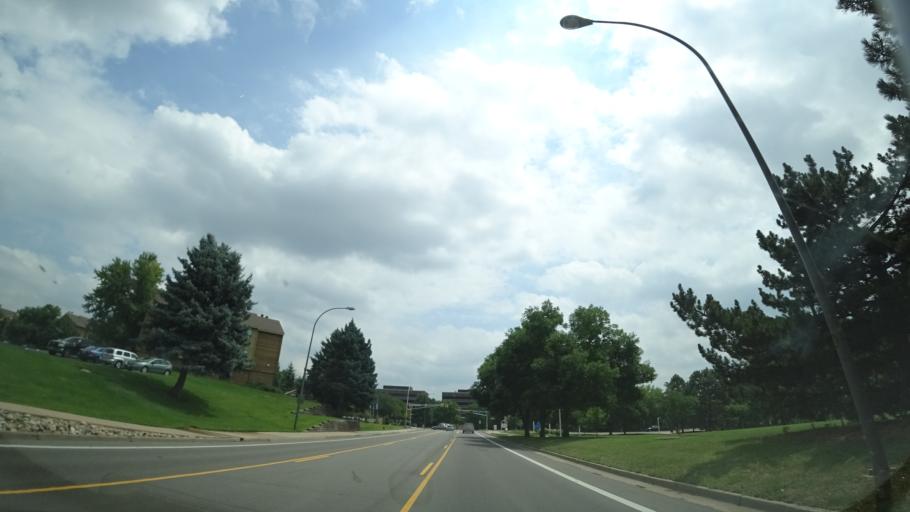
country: US
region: Colorado
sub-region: Jefferson County
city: West Pleasant View
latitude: 39.7188
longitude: -105.1367
